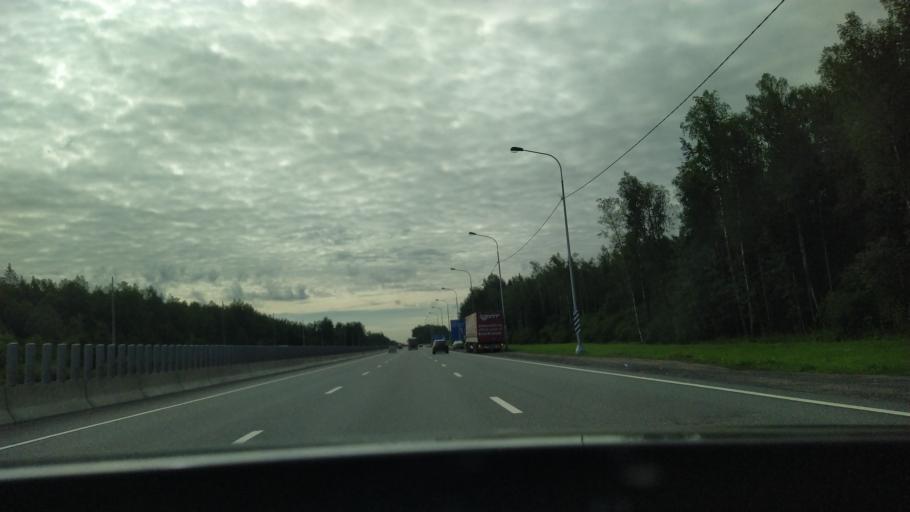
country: RU
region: Leningrad
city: Ul'yanovka
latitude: 59.6018
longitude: 30.7645
